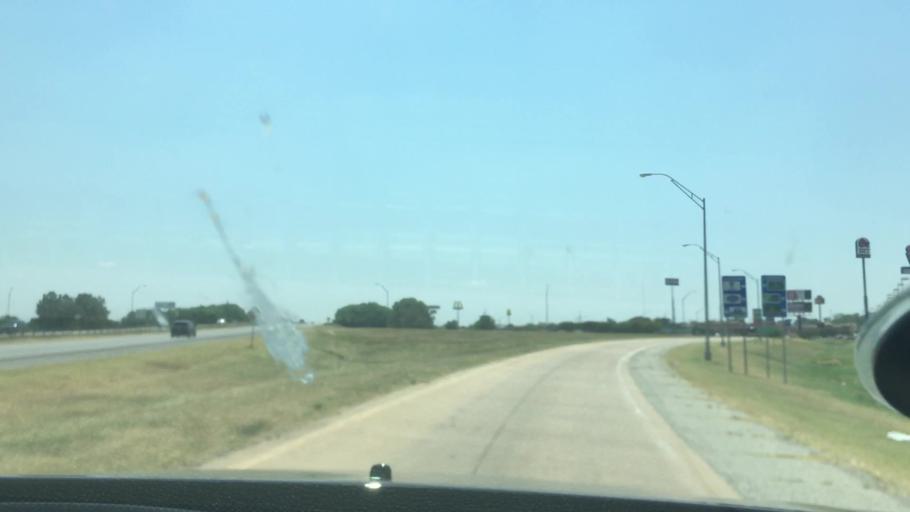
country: US
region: Oklahoma
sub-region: Bryan County
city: Durant
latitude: 34.0011
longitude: -96.4027
